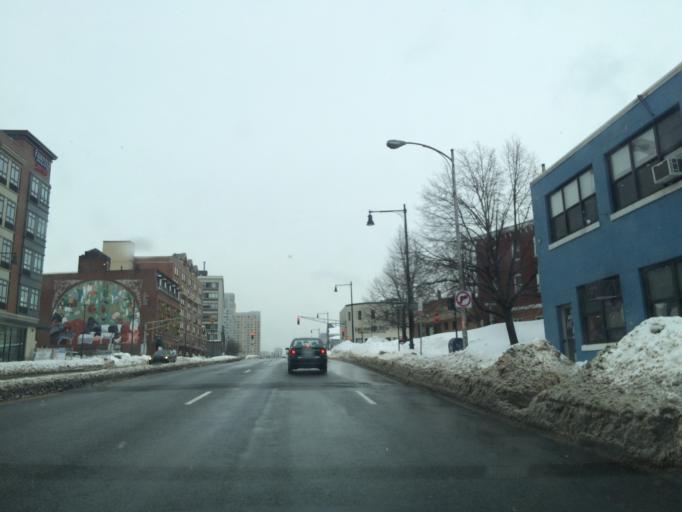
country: US
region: Massachusetts
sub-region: Middlesex County
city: Somerville
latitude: 42.3729
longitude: -71.0804
